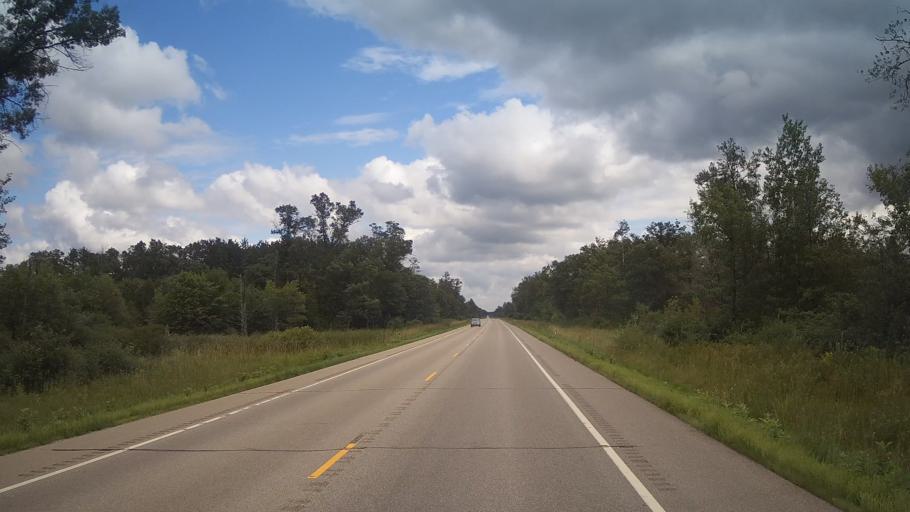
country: US
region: Wisconsin
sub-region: Adams County
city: Friendship
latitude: 44.0254
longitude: -89.7199
